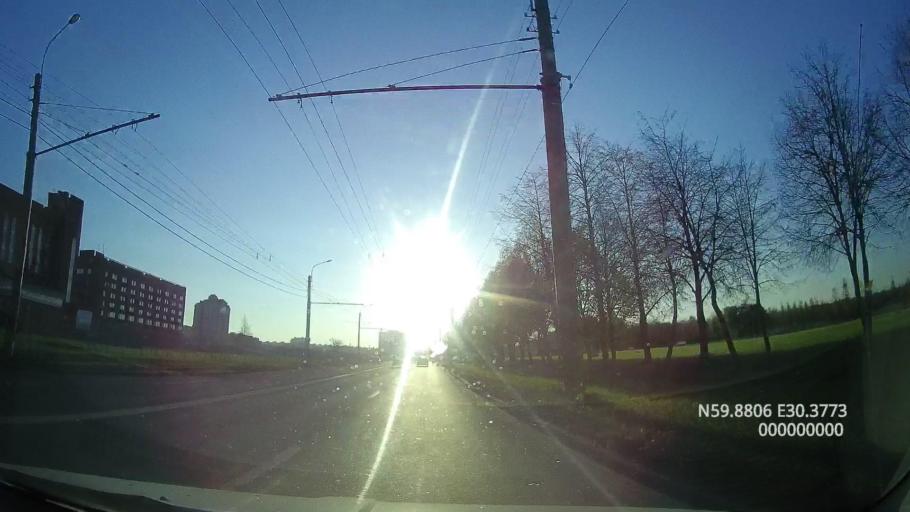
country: RU
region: St.-Petersburg
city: Kupchino
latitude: 59.8804
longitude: 30.3768
